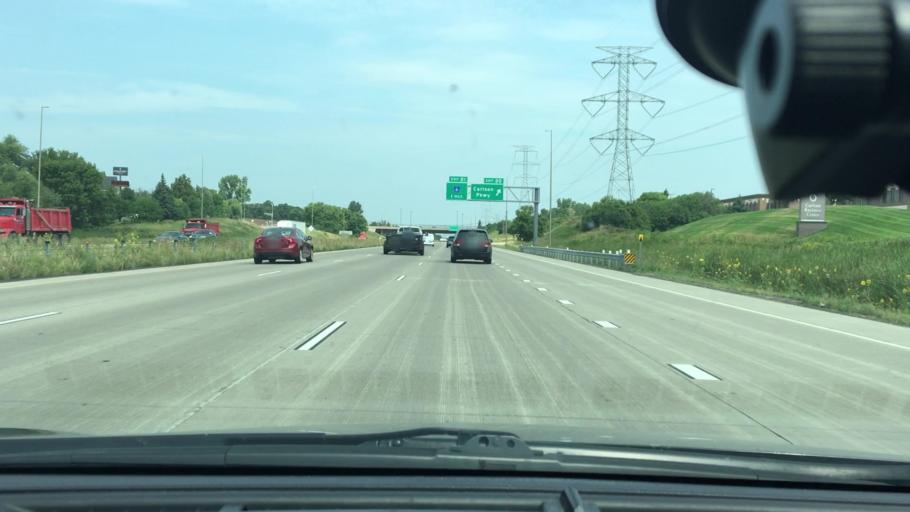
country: US
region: Minnesota
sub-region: Hennepin County
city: Plymouth
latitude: 44.9784
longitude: -93.4600
